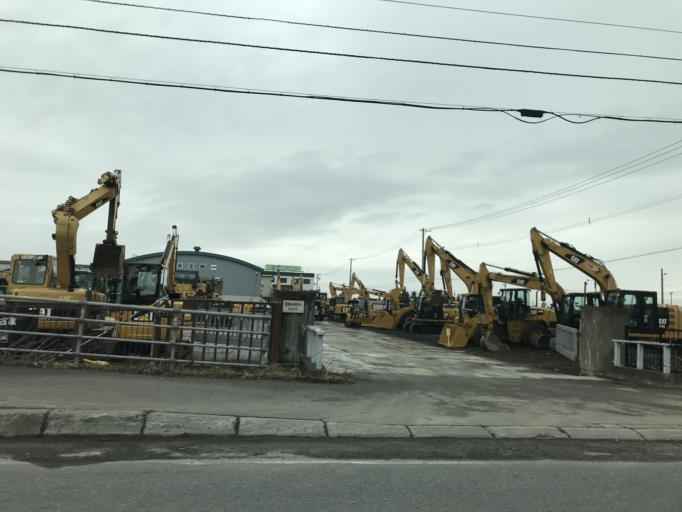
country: JP
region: Hokkaido
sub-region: Asahikawa-shi
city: Asahikawa
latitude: 43.8218
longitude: 142.4119
